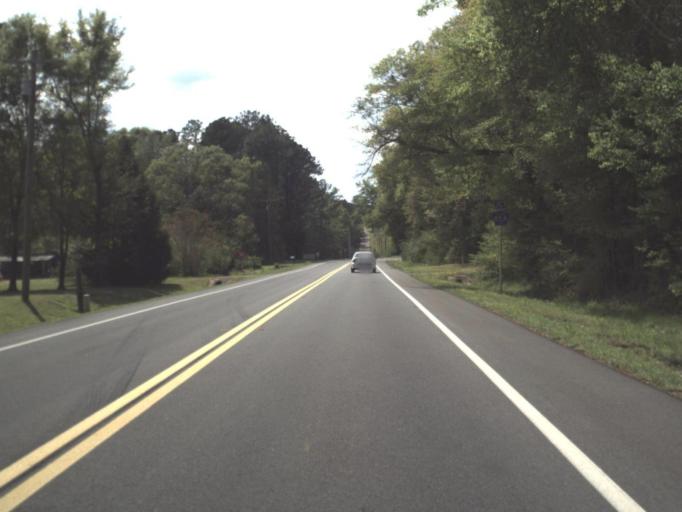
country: US
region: Alabama
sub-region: Covington County
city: Florala
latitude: 30.9634
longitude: -86.4381
